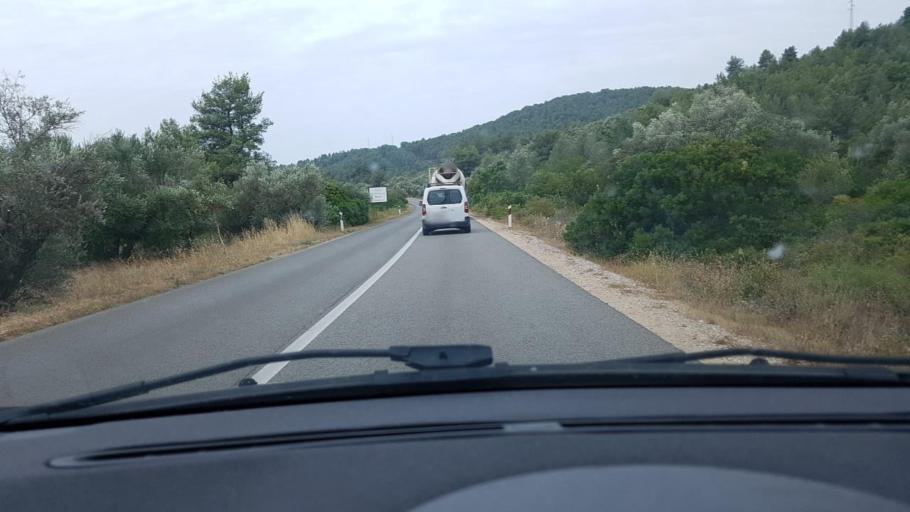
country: HR
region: Dubrovacko-Neretvanska
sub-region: Grad Dubrovnik
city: Vela Luka
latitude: 42.9490
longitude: 16.7612
